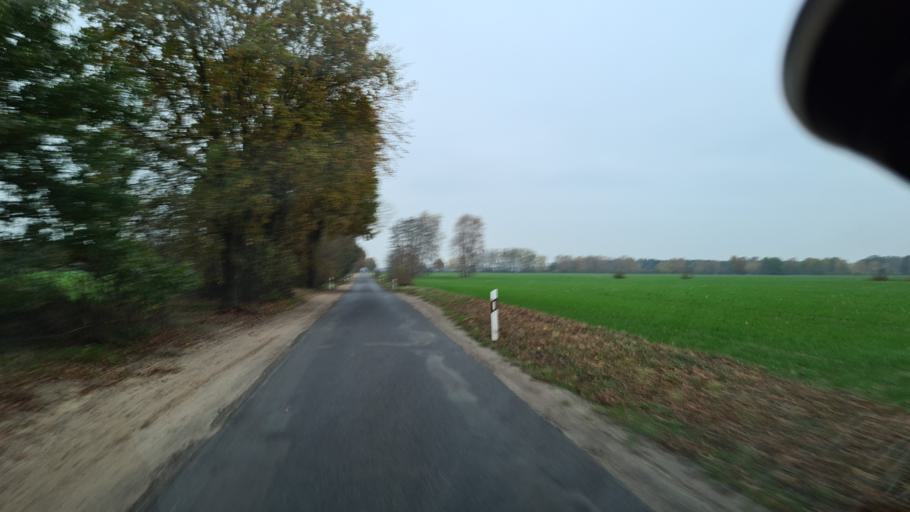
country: DE
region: Brandenburg
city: Lindow
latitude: 52.9261
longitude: 13.0029
